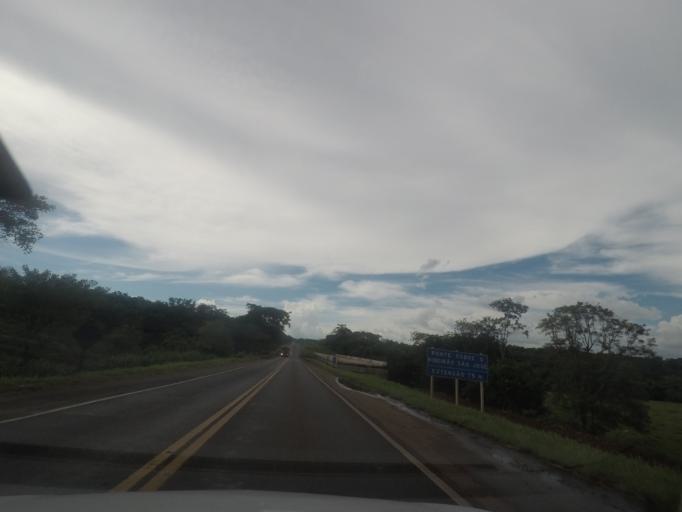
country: BR
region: Minas Gerais
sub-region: Prata
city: Prata
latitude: -19.3483
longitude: -48.8978
